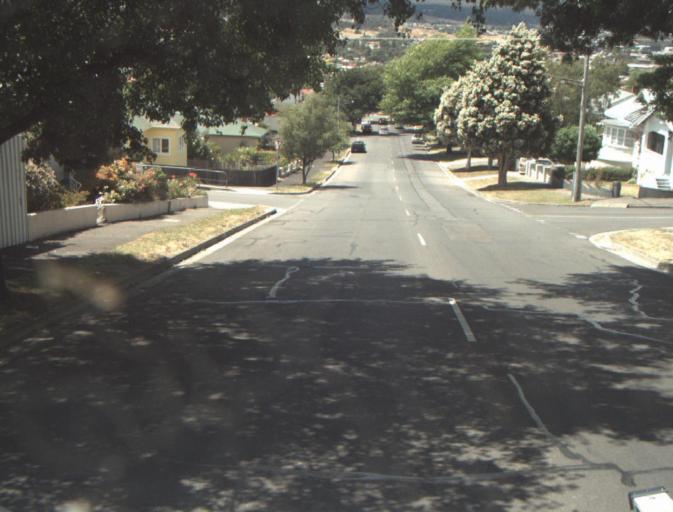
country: AU
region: Tasmania
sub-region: Launceston
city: East Launceston
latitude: -41.4451
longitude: 147.1528
